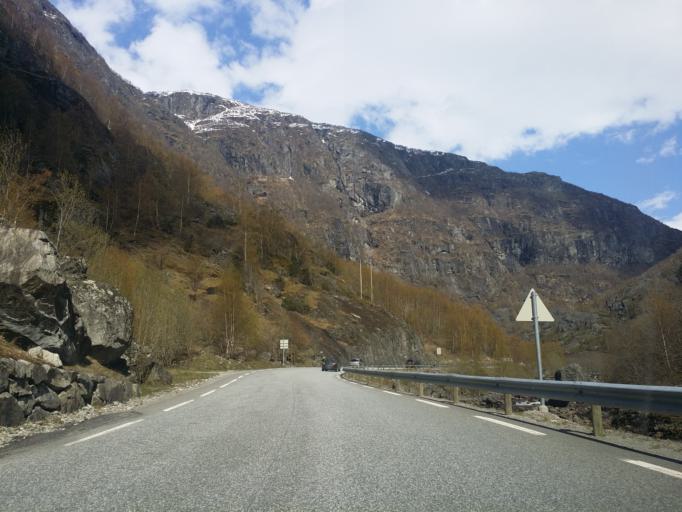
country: NO
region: Hordaland
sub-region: Eidfjord
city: Eidfjord
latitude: 60.4177
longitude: 7.1665
